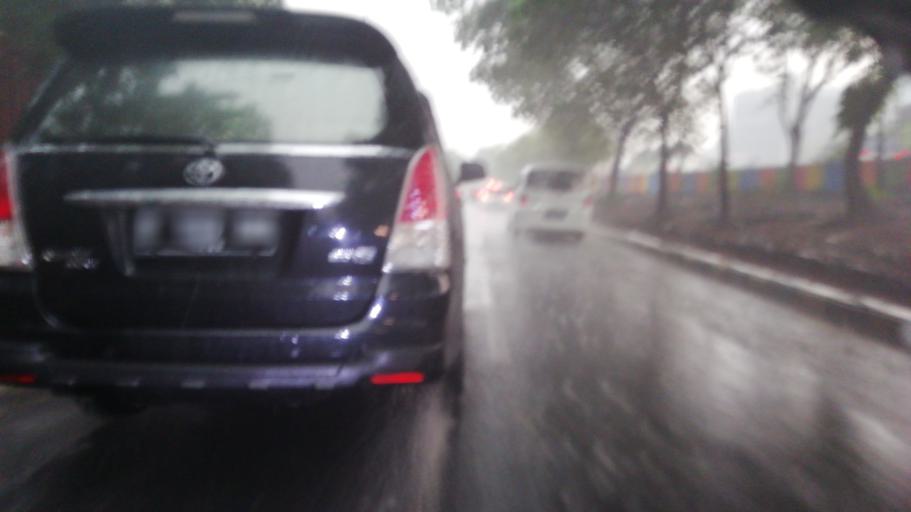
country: ID
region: Jakarta Raya
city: Jakarta
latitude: -6.3043
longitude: 106.8471
